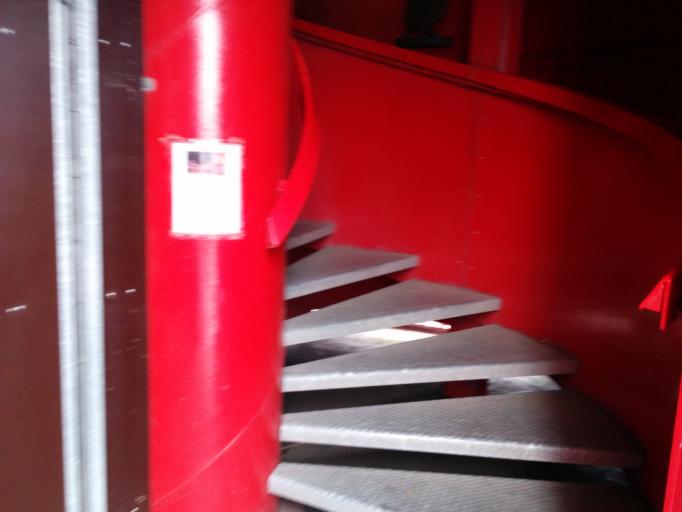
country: DE
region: North Rhine-Westphalia
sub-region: Regierungsbezirk Dusseldorf
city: Moers
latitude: 51.4790
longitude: 6.6506
